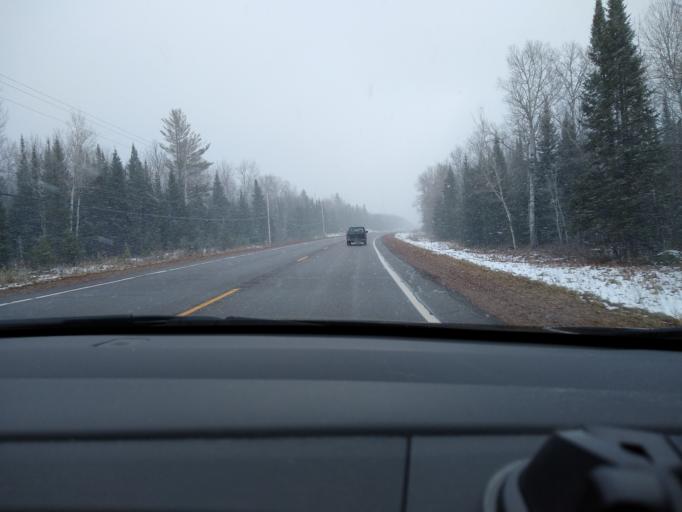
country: US
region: Wisconsin
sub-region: Florence County
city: Florence
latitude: 46.0547
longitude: -88.0638
